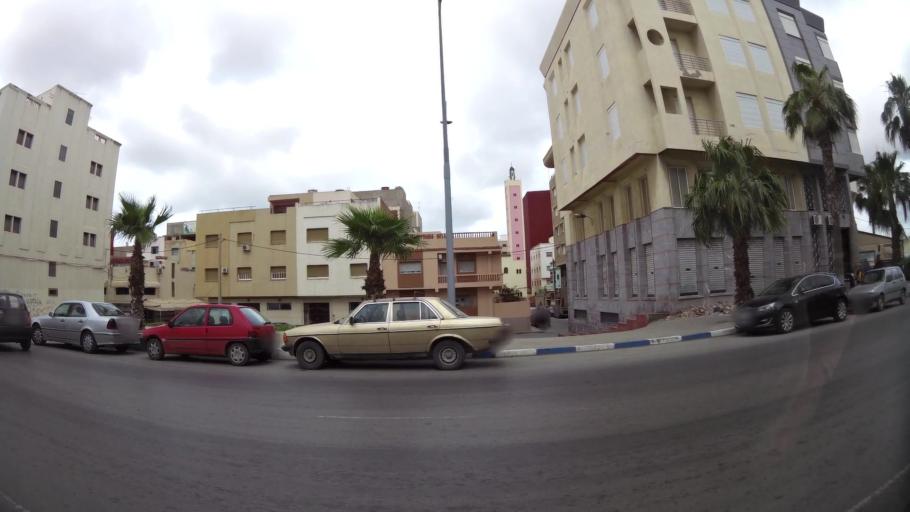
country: MA
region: Oriental
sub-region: Nador
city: Nador
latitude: 35.1612
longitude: -2.9309
